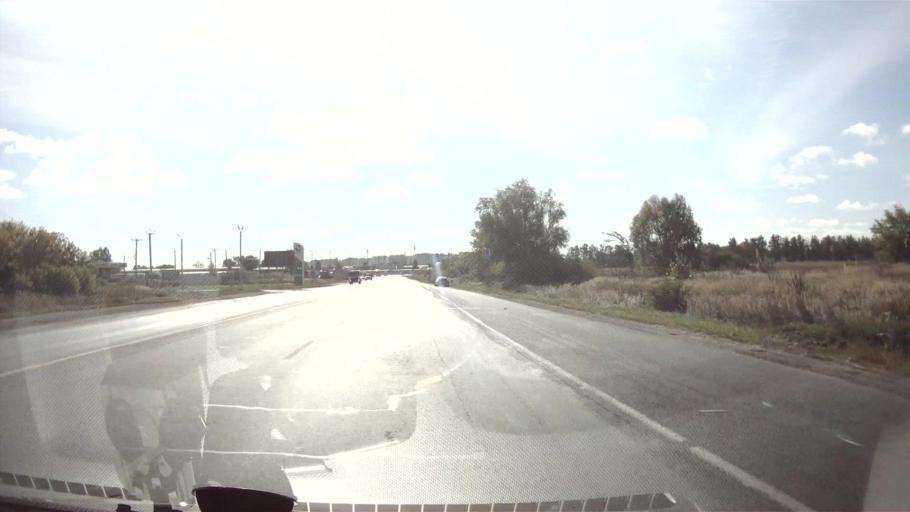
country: RU
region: Ulyanovsk
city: Isheyevka
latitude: 54.2956
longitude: 48.2498
